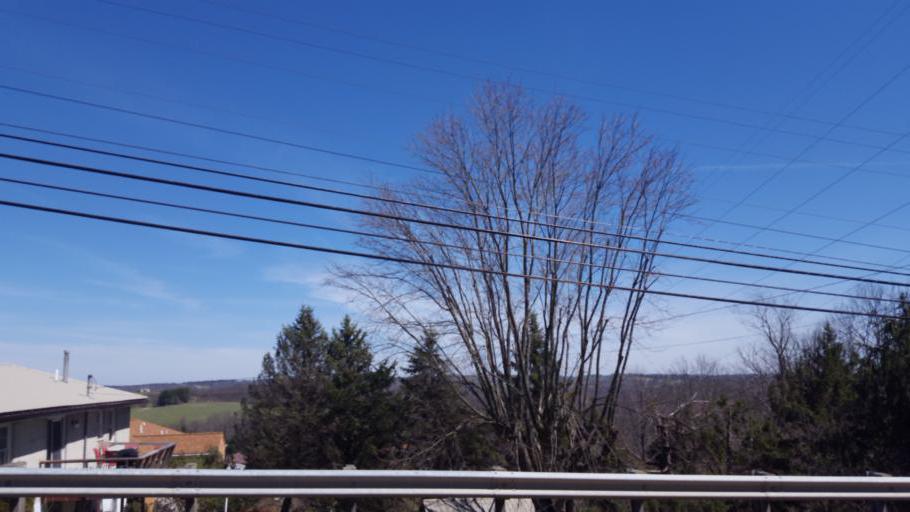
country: US
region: Ohio
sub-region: Belmont County
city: Saint Clairsville
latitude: 40.0759
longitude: -80.8652
